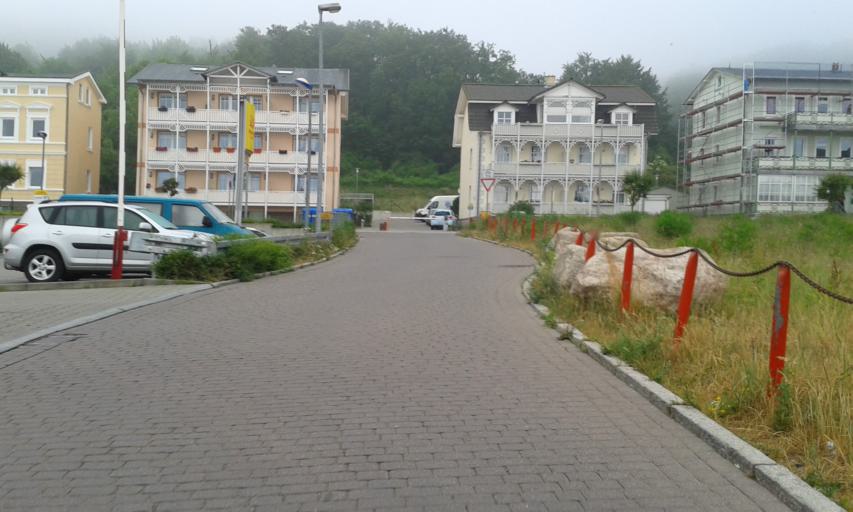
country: DE
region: Mecklenburg-Vorpommern
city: Sassnitz
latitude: 54.5184
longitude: 13.6473
